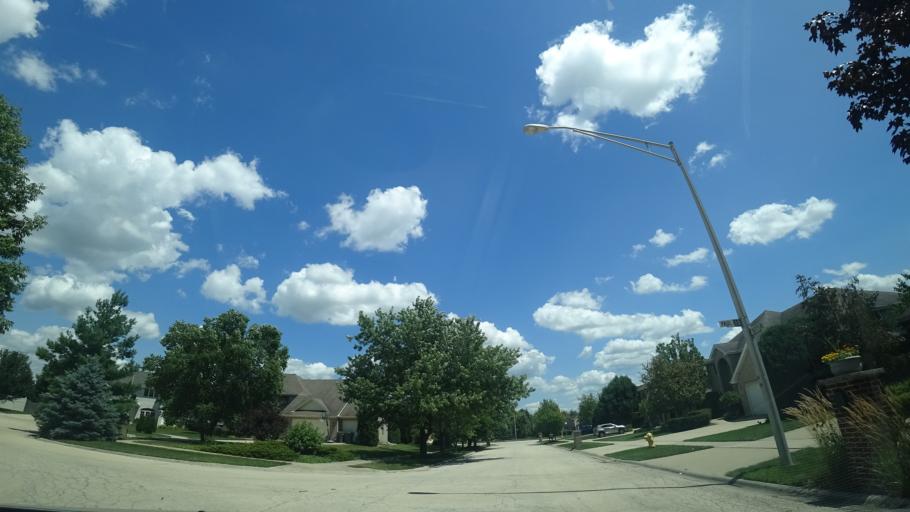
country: US
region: Illinois
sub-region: Cook County
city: Orland Hills
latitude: 41.5852
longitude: -87.8868
